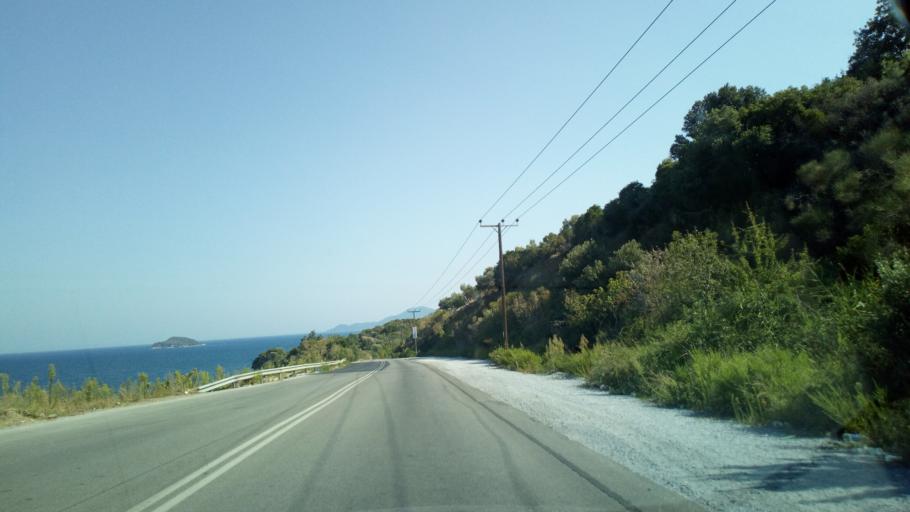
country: GR
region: Central Macedonia
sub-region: Nomos Thessalonikis
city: Stavros
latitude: 40.6323
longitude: 23.7619
